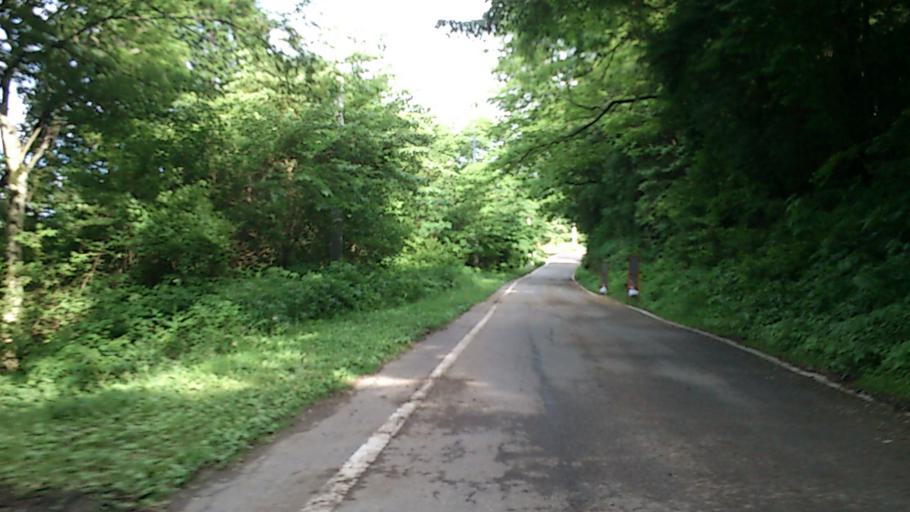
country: JP
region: Nagano
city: Saku
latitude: 36.2460
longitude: 138.6211
